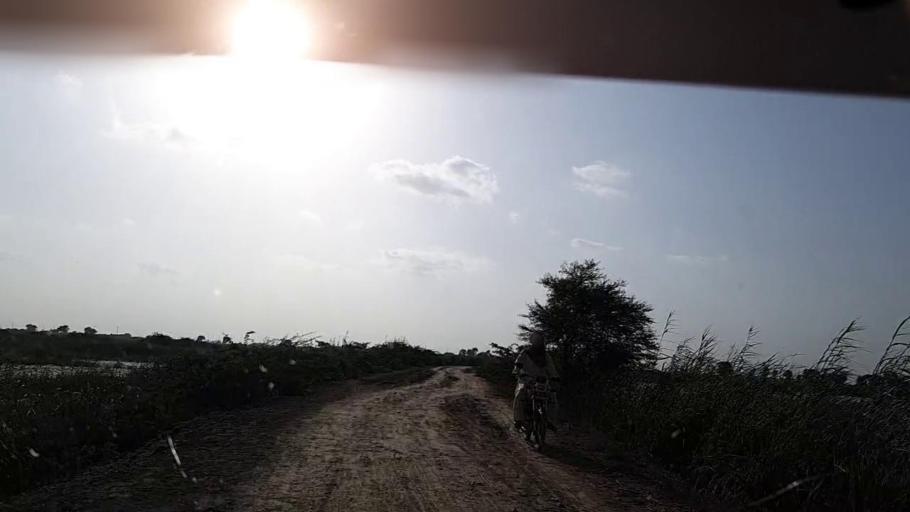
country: PK
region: Sindh
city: Badin
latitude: 24.5586
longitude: 68.8897
